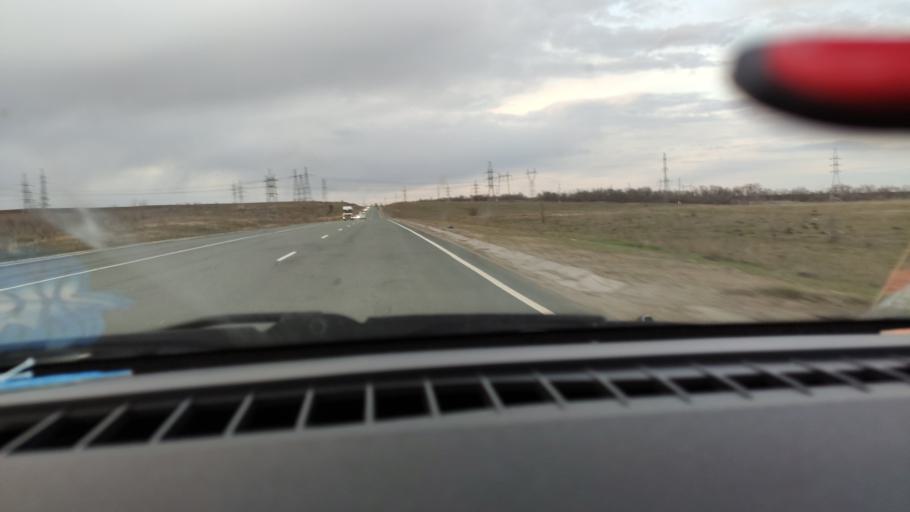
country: RU
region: Saratov
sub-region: Saratovskiy Rayon
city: Saratov
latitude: 51.7653
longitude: 46.0763
